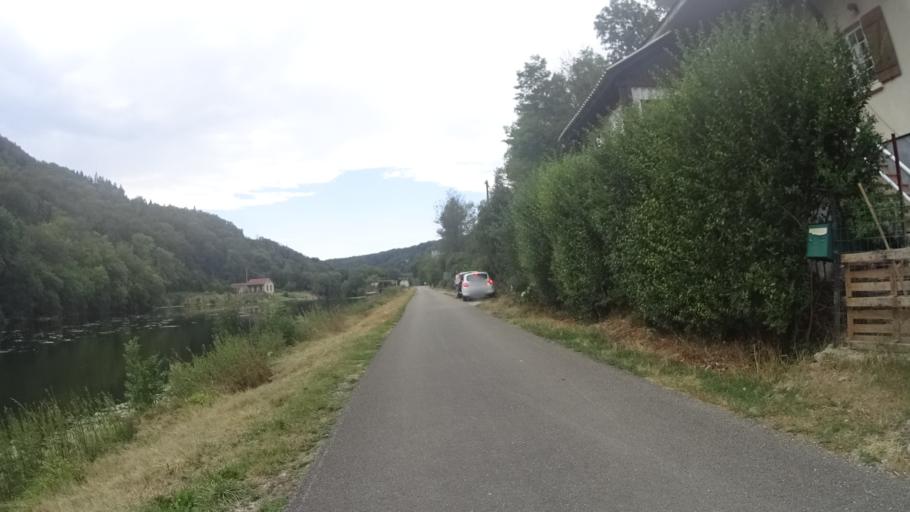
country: FR
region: Franche-Comte
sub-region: Departement du Doubs
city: Baume-les-Dames
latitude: 47.3299
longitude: 6.3077
